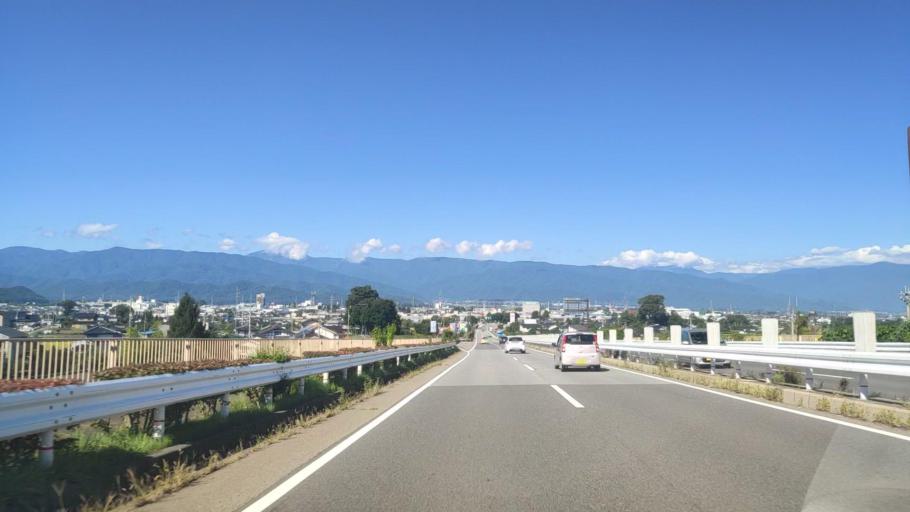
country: JP
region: Nagano
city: Shiojiri
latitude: 36.1169
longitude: 137.9739
